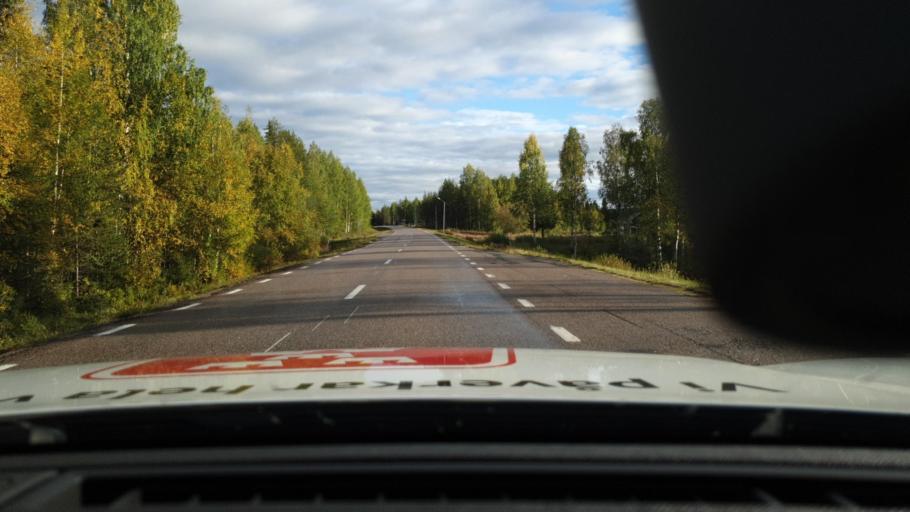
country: SE
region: Norrbotten
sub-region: Overkalix Kommun
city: OEverkalix
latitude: 66.6283
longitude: 22.7348
